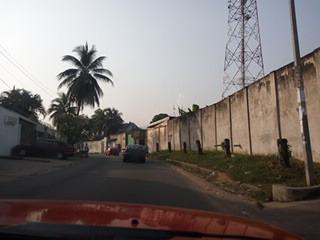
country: CI
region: Lagunes
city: Abobo
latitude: 5.3830
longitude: -3.9922
